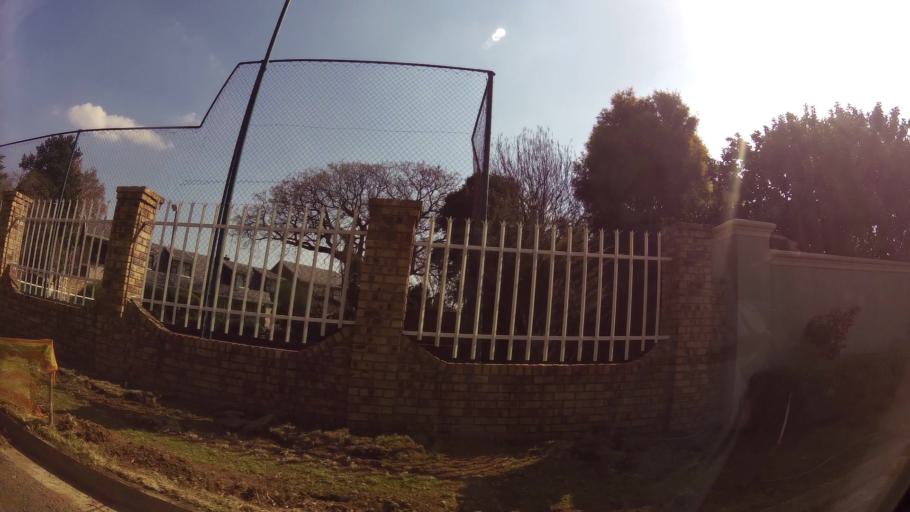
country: ZA
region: Gauteng
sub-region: Ekurhuleni Metropolitan Municipality
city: Benoni
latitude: -26.1839
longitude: 28.2922
